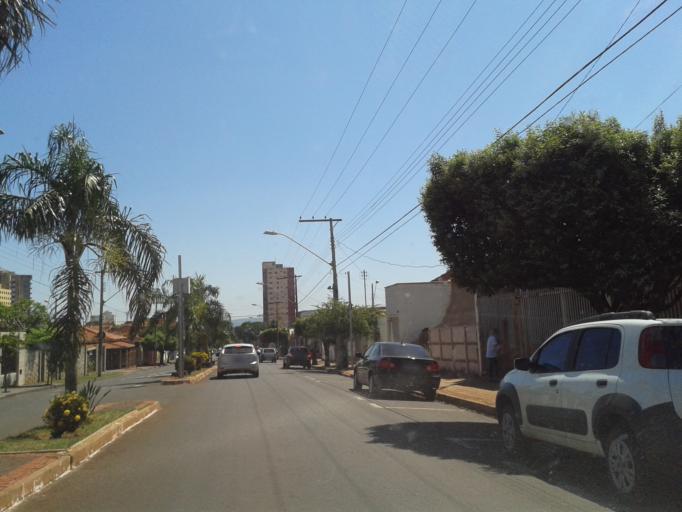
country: BR
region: Minas Gerais
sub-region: Ituiutaba
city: Ituiutaba
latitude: -18.9788
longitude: -49.4590
